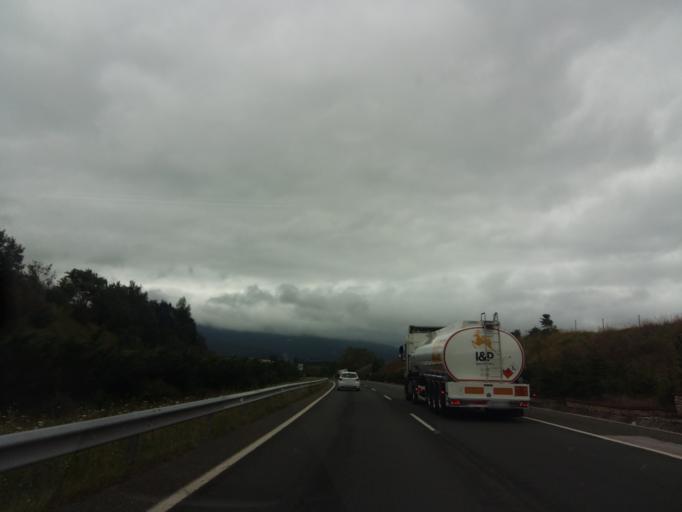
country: ES
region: Navarre
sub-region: Provincia de Navarra
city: Arbizu
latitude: 42.9145
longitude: -2.0327
